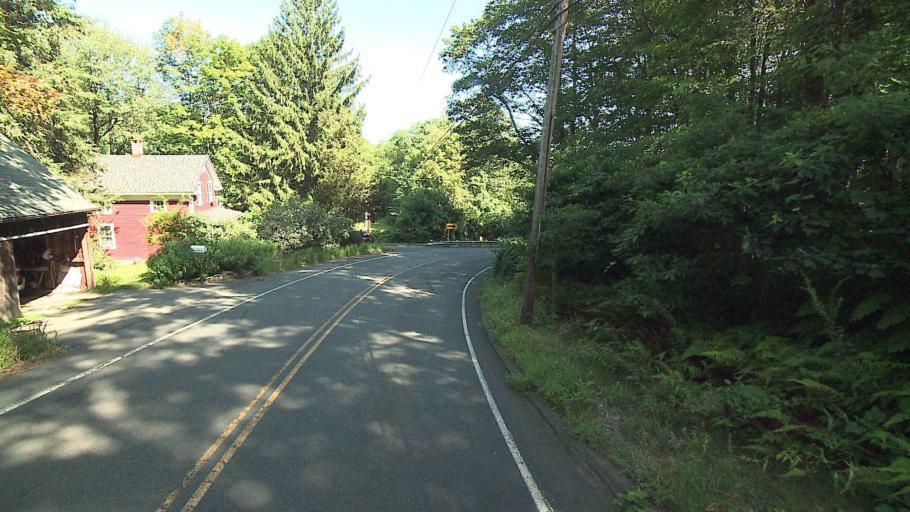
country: US
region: Connecticut
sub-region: Hartford County
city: West Simsbury
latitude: 41.8833
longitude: -72.8715
